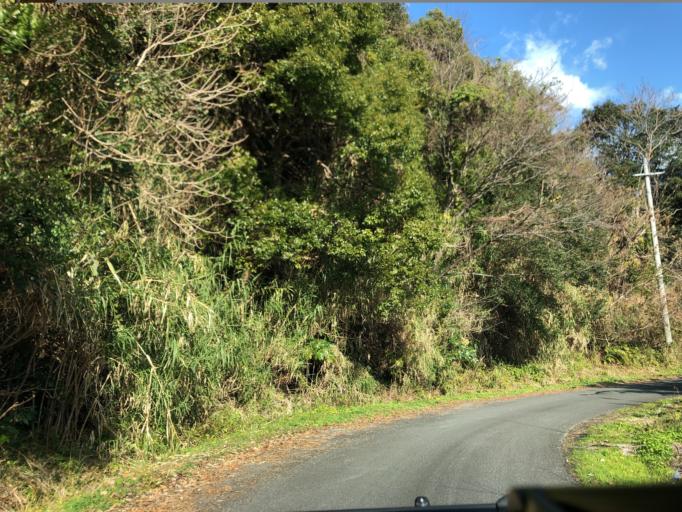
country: JP
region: Kochi
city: Sukumo
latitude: 32.9115
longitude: 132.6972
